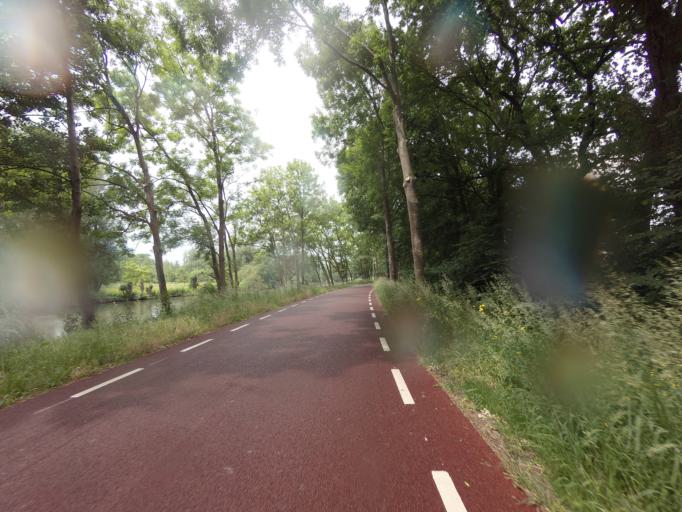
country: NL
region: Utrecht
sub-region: Stichtse Vecht
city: Maarssen
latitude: 52.1227
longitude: 5.0744
